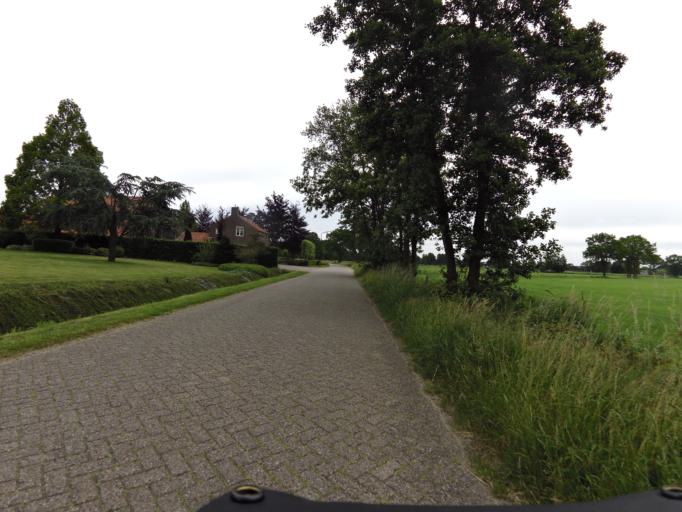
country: NL
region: North Brabant
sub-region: Gemeente Hilvarenbeek
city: Hilvarenbeek
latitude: 51.4864
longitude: 5.1094
